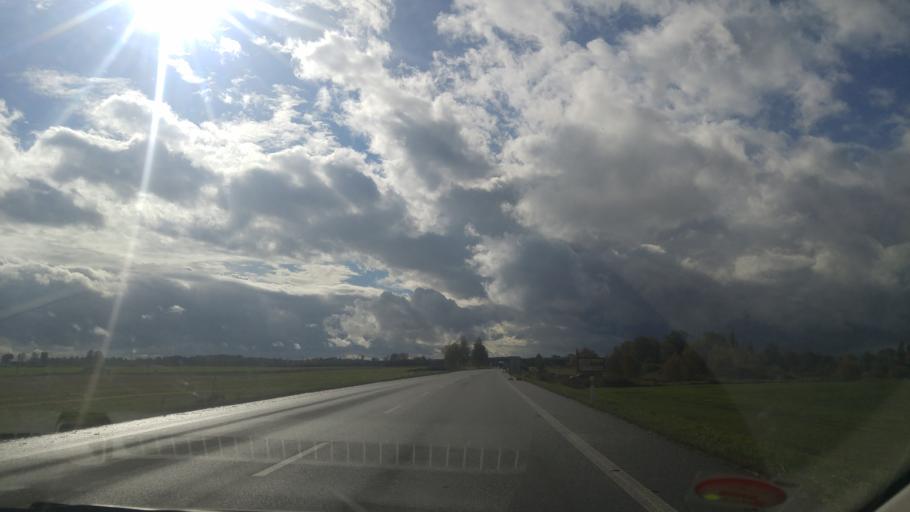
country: CZ
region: Jihocesky
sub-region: Okres Tabor
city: Veseli nad Luznici
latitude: 49.1772
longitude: 14.6884
